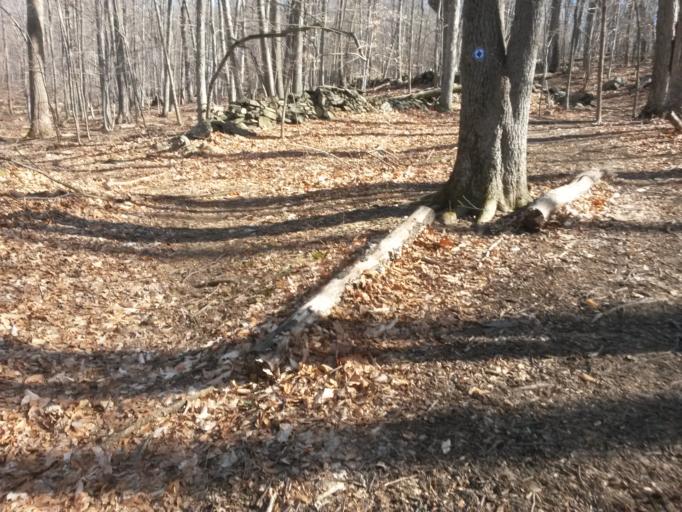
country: US
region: New York
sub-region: Westchester County
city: Yorktown Heights
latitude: 41.2526
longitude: -73.7703
